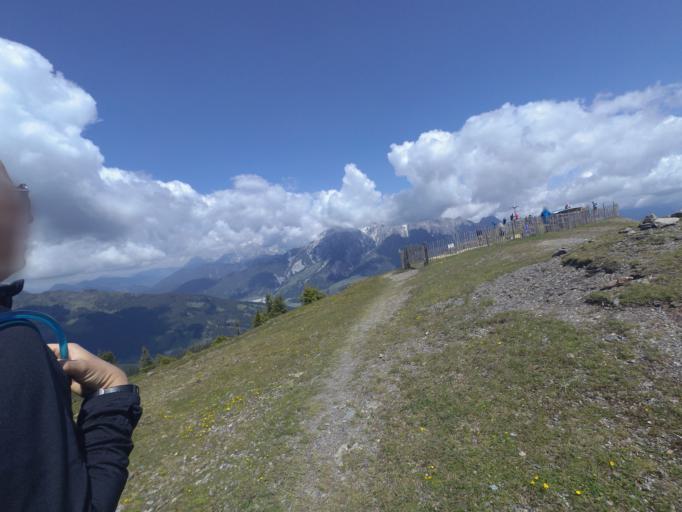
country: AT
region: Salzburg
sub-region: Politischer Bezirk Zell am See
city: Viehhofen
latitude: 47.4022
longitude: 12.7020
